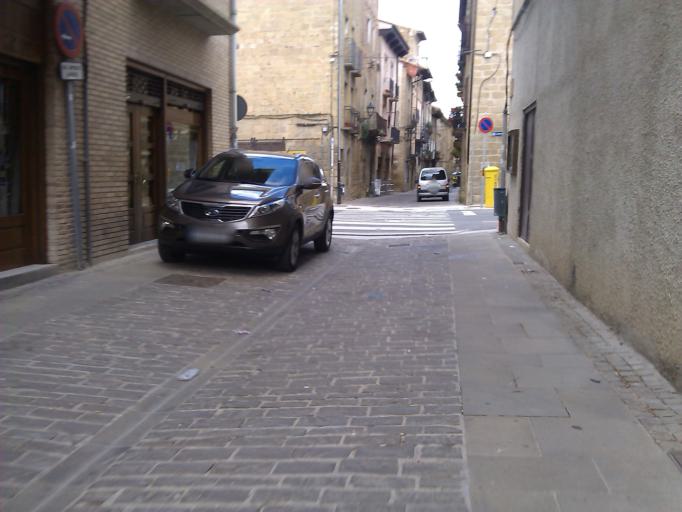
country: ES
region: Navarre
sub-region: Provincia de Navarra
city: Puente la Reina
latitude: 42.6725
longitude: -1.8126
